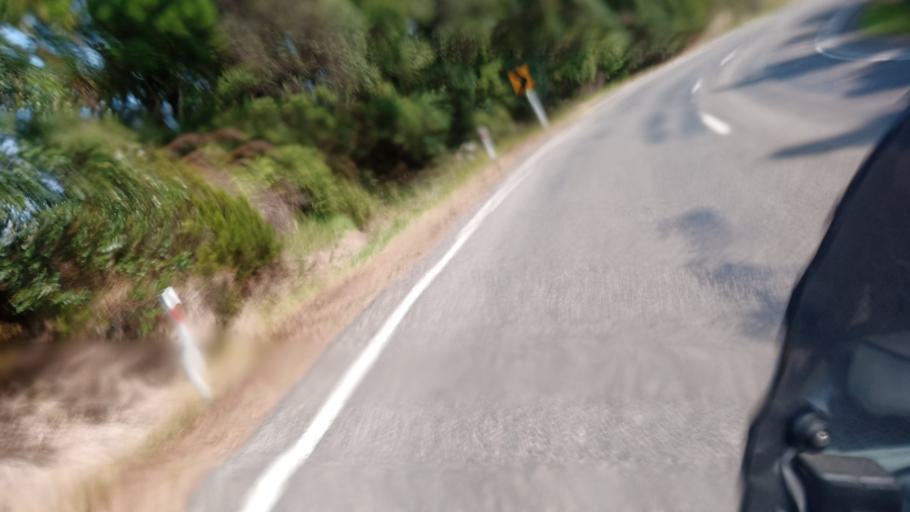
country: NZ
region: Bay of Plenty
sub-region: Opotiki District
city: Opotiki
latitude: -37.5932
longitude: 178.2216
